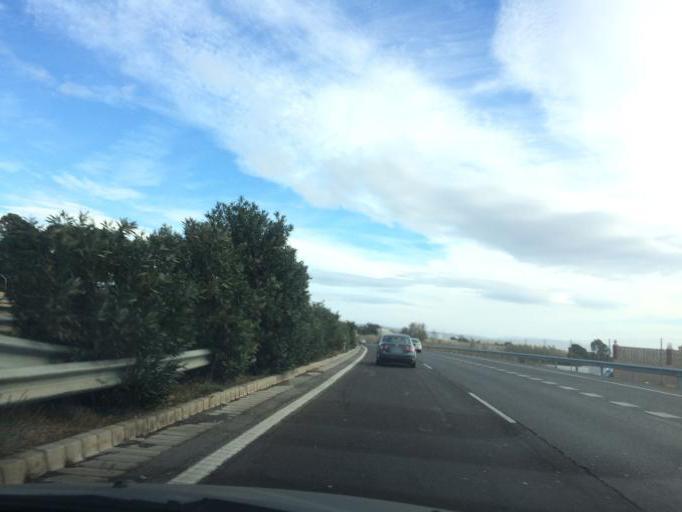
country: ES
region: Andalusia
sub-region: Provincia de Almeria
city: Viator
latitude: 36.8437
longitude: -2.3994
